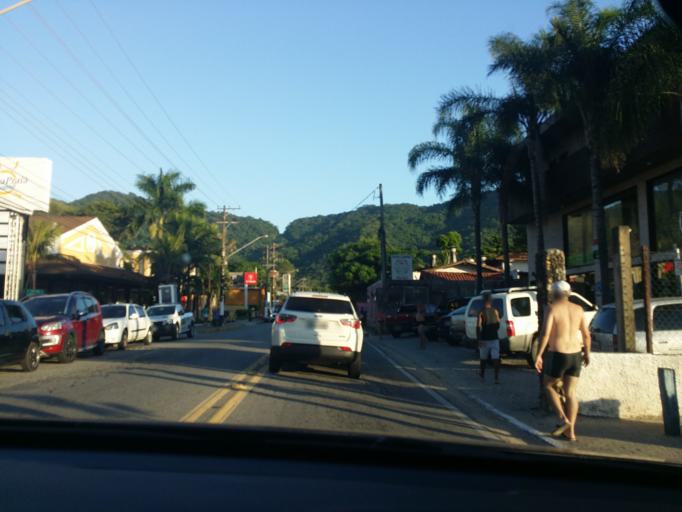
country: BR
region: Sao Paulo
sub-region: Sao Sebastiao
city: Sao Sebastiao
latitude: -23.7848
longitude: -45.6270
